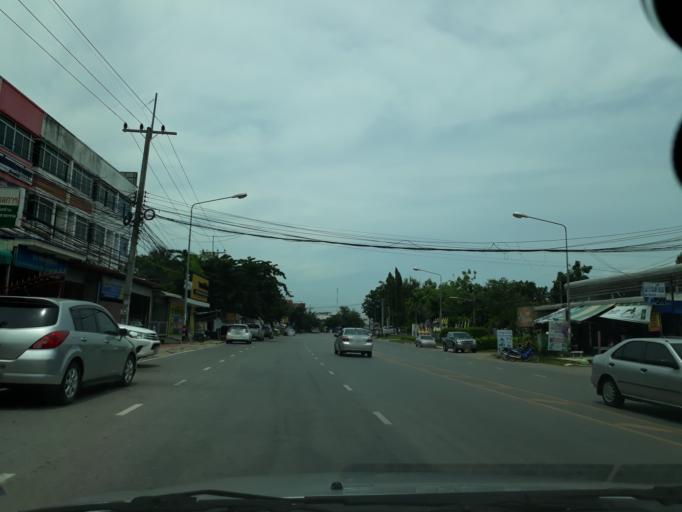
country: TH
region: Khon Kaen
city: Khon Kaen
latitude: 16.4333
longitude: 102.8658
